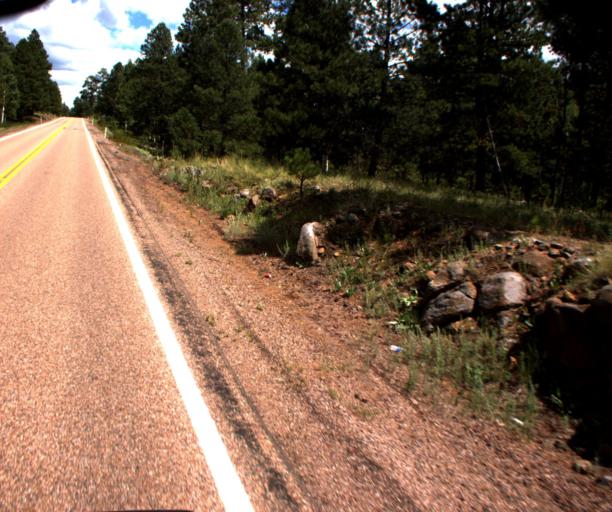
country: US
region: Arizona
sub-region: Navajo County
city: Pinetop-Lakeside
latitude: 34.0238
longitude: -109.6440
